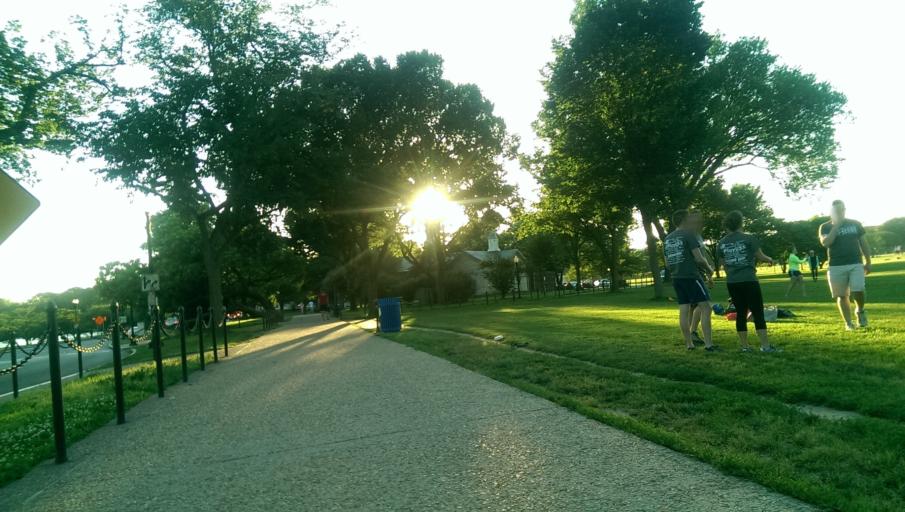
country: US
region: Washington, D.C.
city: Washington, D.C.
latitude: 38.8878
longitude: -77.0365
